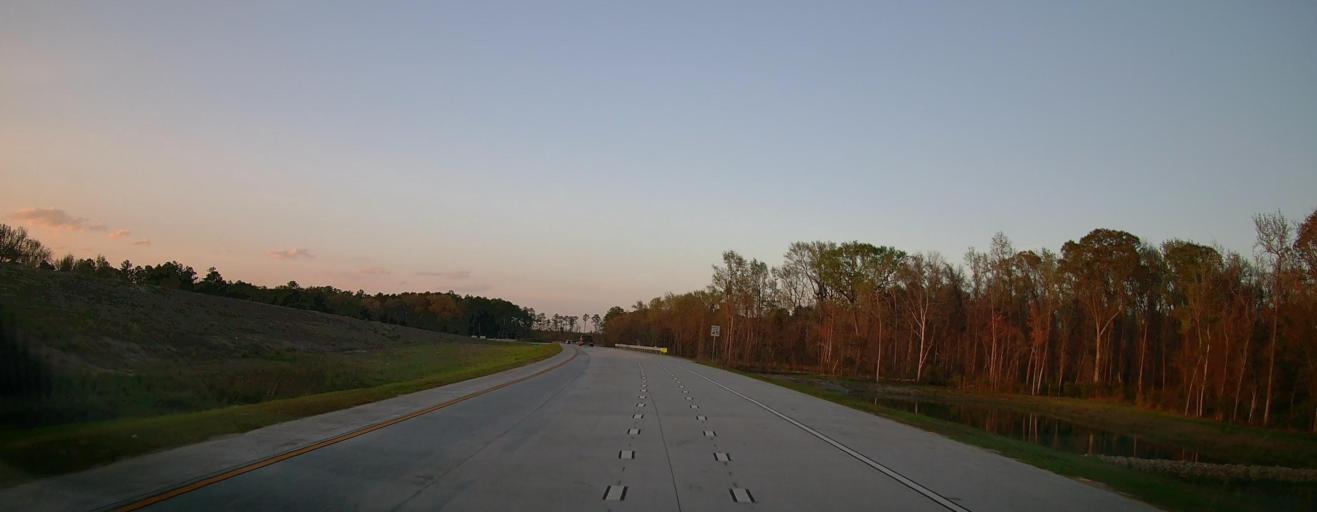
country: US
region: Georgia
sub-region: Chatham County
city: Bloomingdale
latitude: 32.1364
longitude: -81.3080
